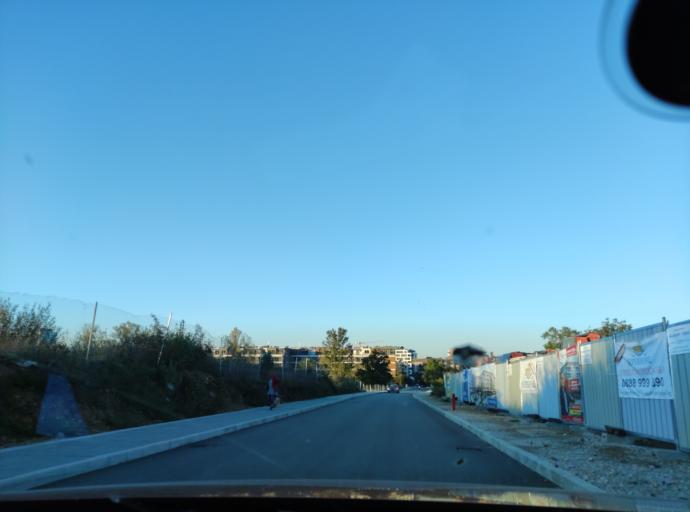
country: BG
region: Sofia-Capital
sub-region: Stolichna Obshtina
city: Sofia
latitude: 42.6575
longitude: 23.2922
